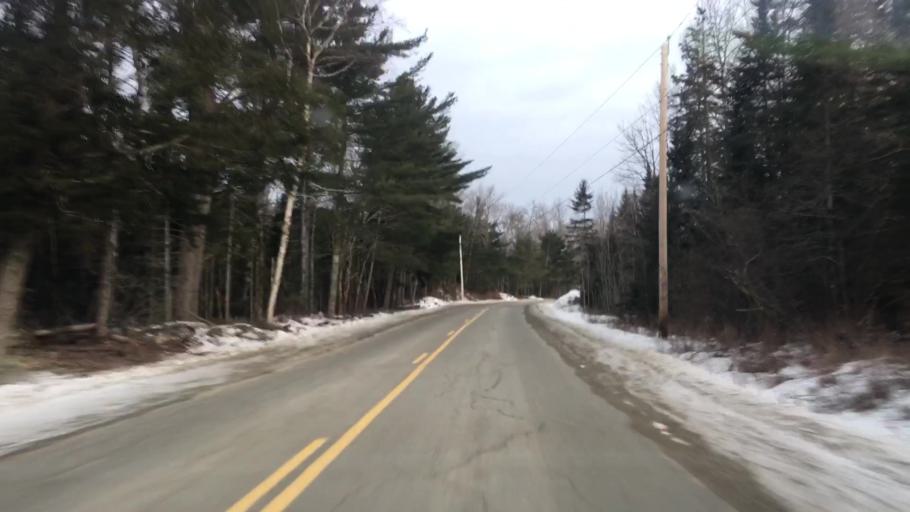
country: US
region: Maine
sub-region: Hancock County
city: Franklin
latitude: 44.7572
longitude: -68.3243
